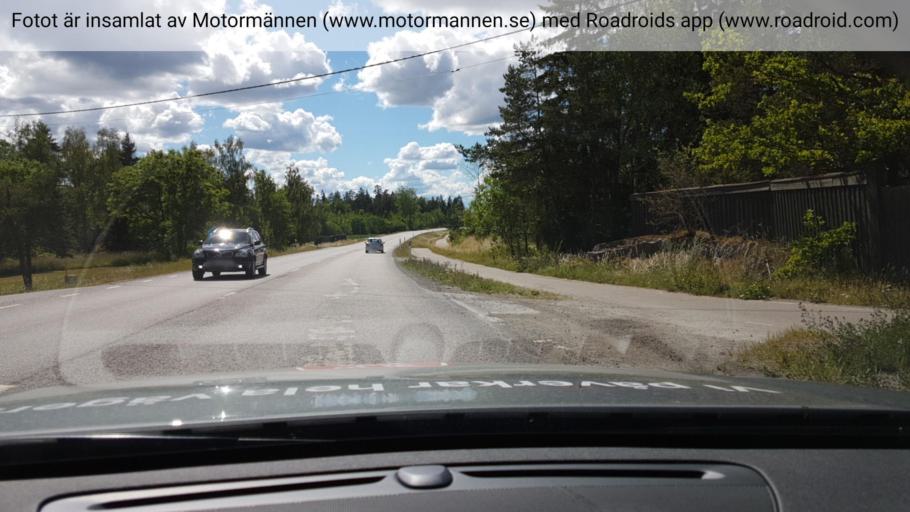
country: SE
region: Uppsala
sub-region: Uppsala Kommun
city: Saevja
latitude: 59.8503
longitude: 17.7859
